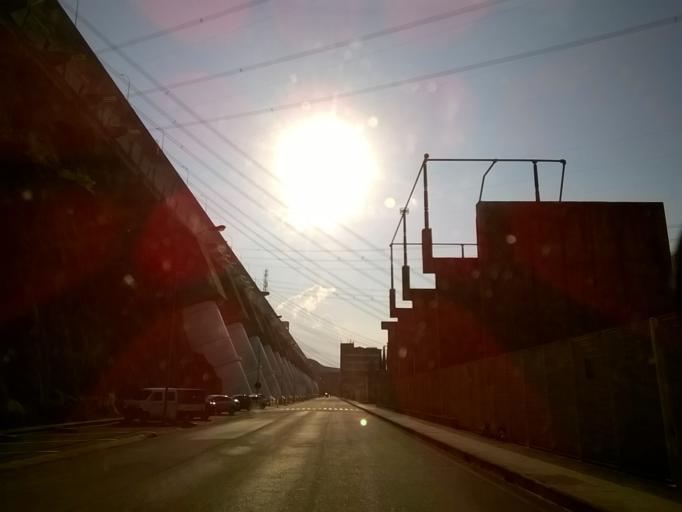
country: PY
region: Alto Parana
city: Ciudad del Este
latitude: -25.4072
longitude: -54.5933
